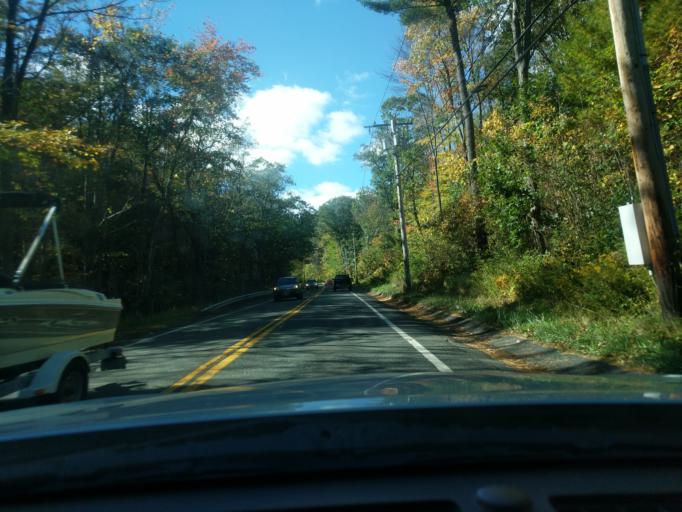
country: US
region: Massachusetts
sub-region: Hampden County
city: Granville
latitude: 42.1704
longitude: -72.8841
